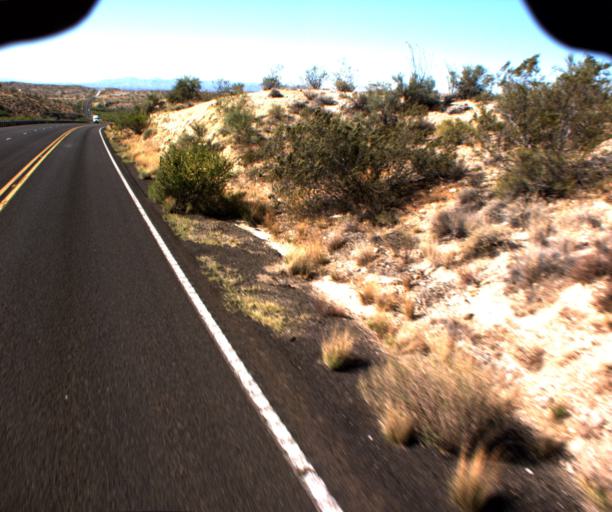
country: US
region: Arizona
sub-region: Mohave County
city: Kingman
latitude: 34.9279
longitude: -113.6588
